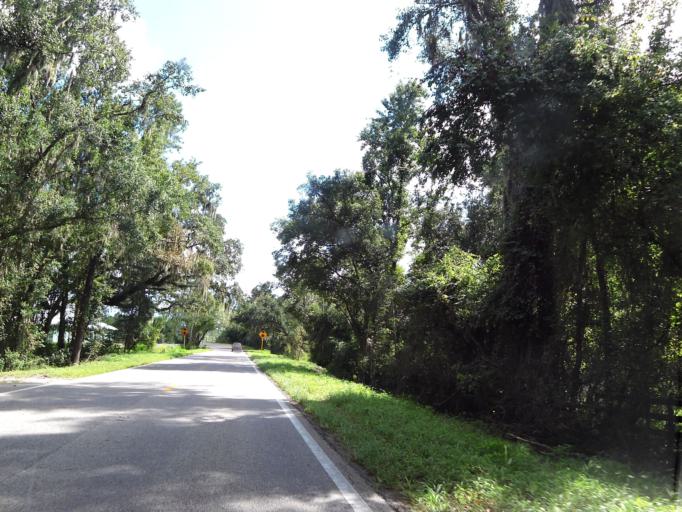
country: US
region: Florida
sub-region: Putnam County
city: East Palatka
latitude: 29.7440
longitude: -81.4755
